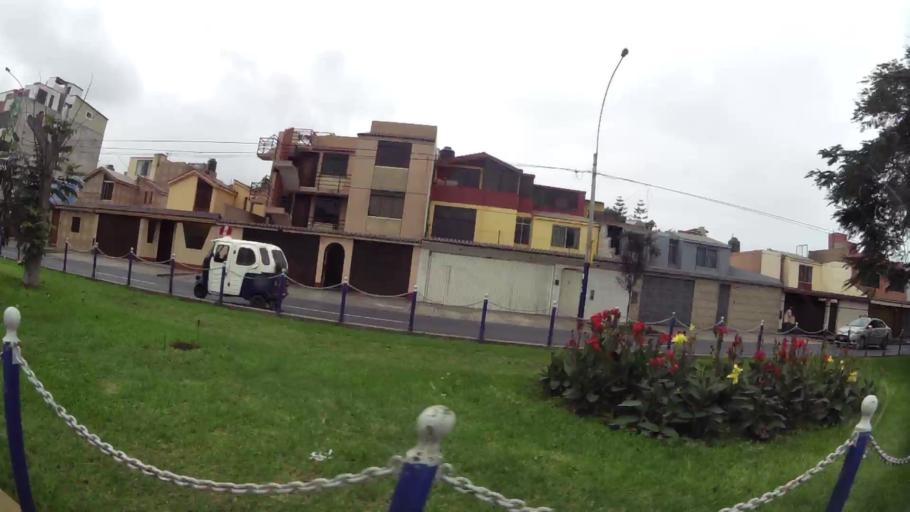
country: PE
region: Lima
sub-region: Lima
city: Surco
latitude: -12.1757
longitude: -77.0062
